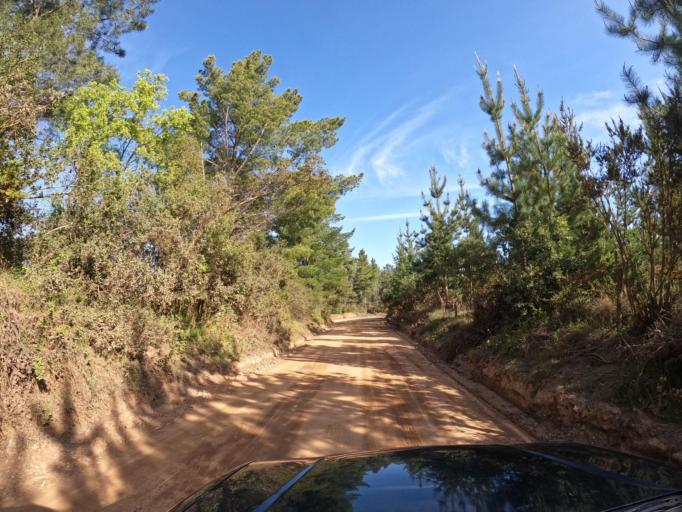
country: CL
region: Biobio
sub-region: Provincia de Biobio
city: La Laja
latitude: -37.1141
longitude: -72.7390
